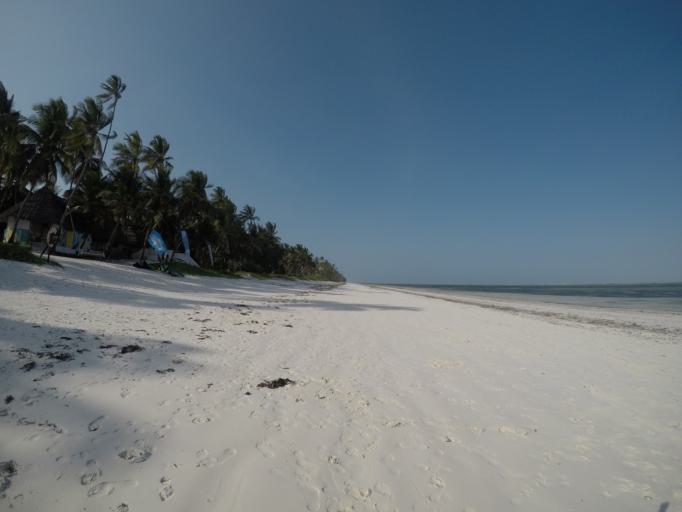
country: TZ
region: Zanzibar Central/South
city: Nganane
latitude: -6.2146
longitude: 39.5338
